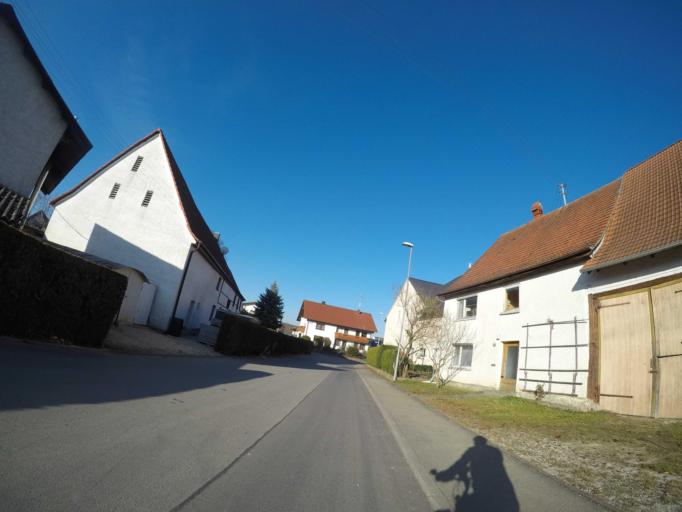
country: DE
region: Baden-Wuerttemberg
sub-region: Tuebingen Region
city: Grundsheim
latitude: 48.1749
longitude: 9.6671
